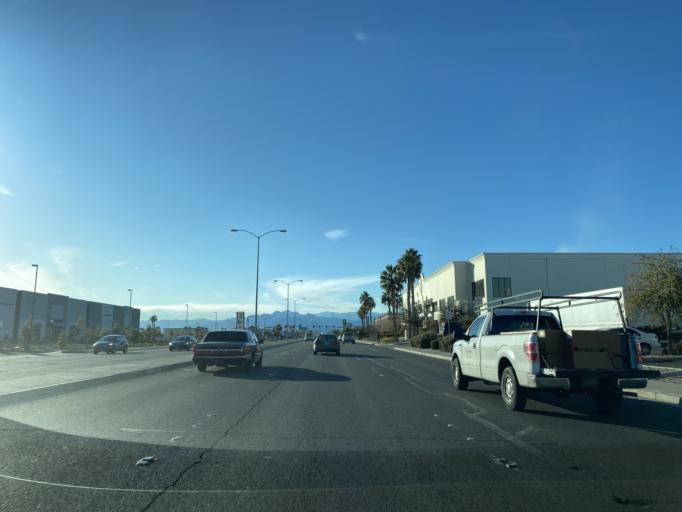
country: US
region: Nevada
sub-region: Clark County
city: Nellis Air Force Base
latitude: 36.2405
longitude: -115.0864
